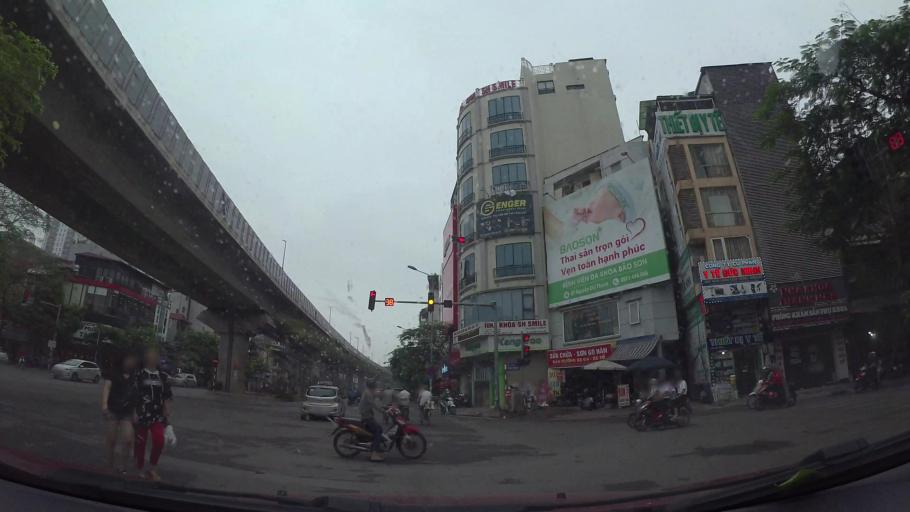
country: VN
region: Ha Noi
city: Dong Da
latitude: 21.0118
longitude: 105.8173
